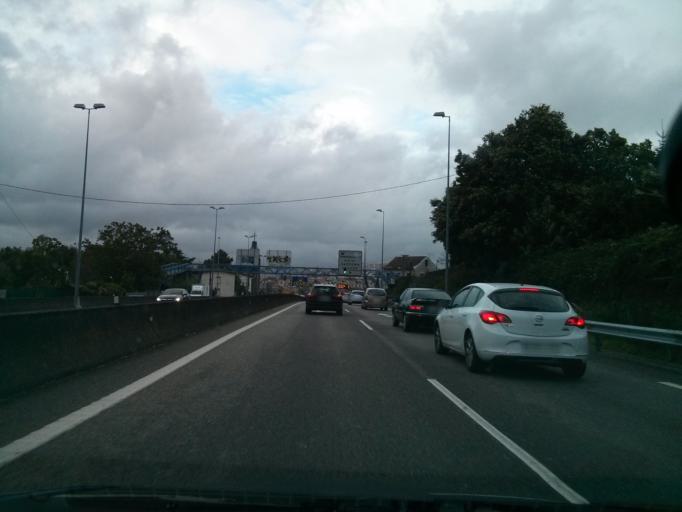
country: ES
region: Galicia
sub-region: Provincia de Pontevedra
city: Vigo
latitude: 42.2125
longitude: -8.6986
